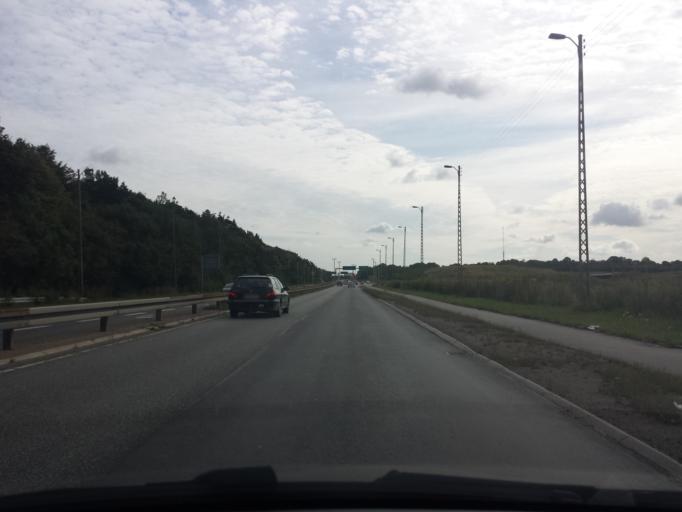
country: DK
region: Capital Region
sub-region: Glostrup Kommune
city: Glostrup
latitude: 55.6921
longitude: 12.4221
